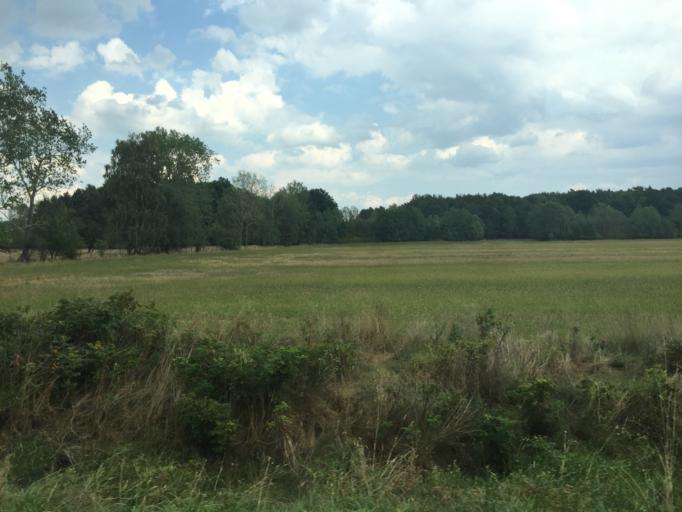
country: DE
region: Saxony
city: Trebendorf
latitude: 51.5227
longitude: 14.5543
